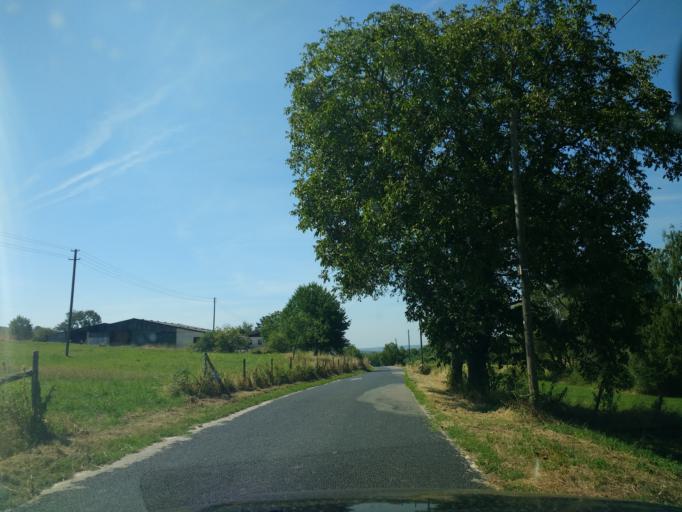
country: DE
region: Rheinland-Pfalz
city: Wincheringen
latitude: 49.6328
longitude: 6.4419
